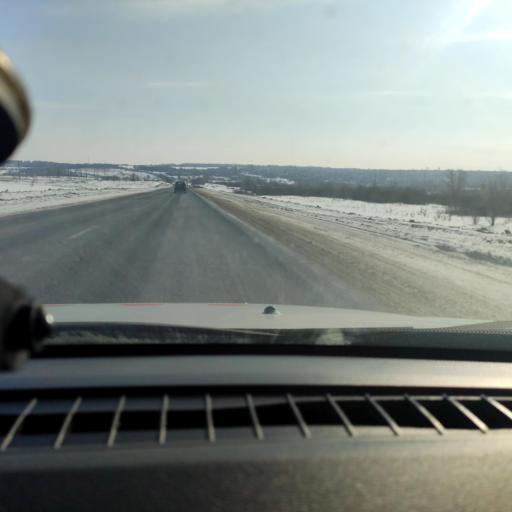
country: RU
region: Samara
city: Smyshlyayevka
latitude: 53.2902
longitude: 50.4605
